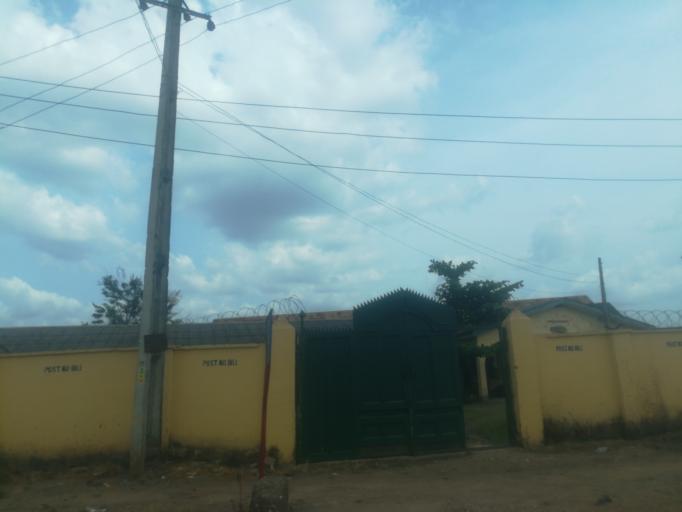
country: NG
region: Ogun
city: Abeokuta
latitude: 7.1351
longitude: 3.3215
